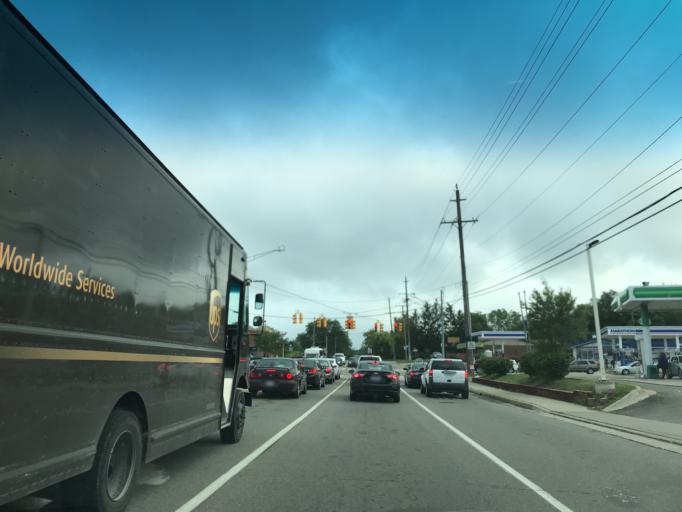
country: US
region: Michigan
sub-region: Washtenaw County
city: Ypsilanti
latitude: 42.2508
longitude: -83.6611
